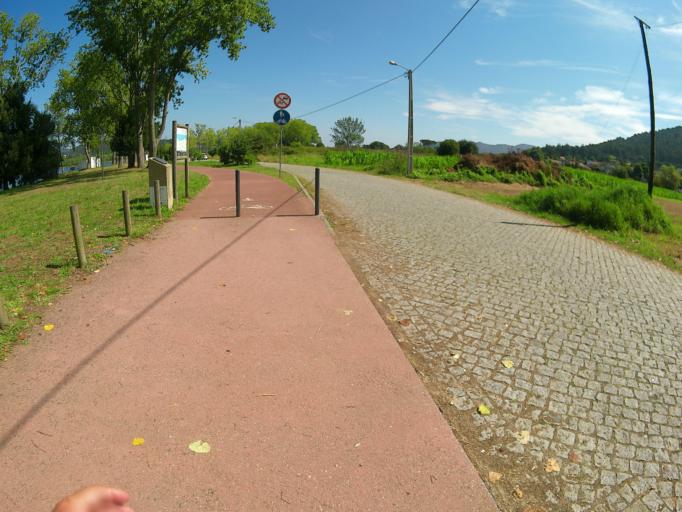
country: ES
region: Galicia
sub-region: Provincia de Pontevedra
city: O Rosal
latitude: 41.9107
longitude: -8.7933
